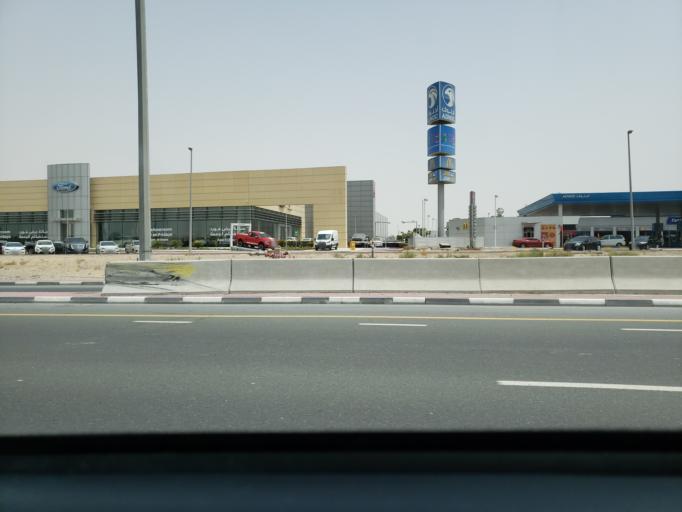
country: AE
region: Ash Shariqah
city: Sharjah
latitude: 25.3468
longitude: 55.4744
